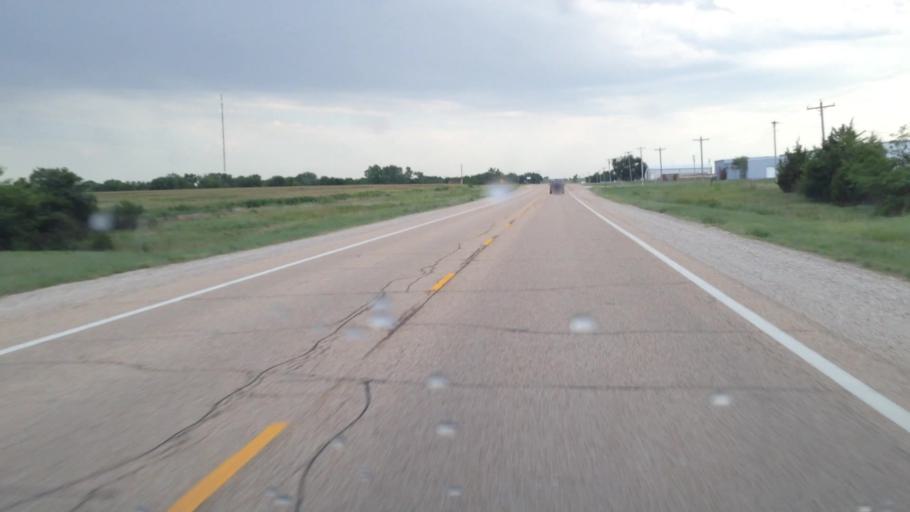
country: US
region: Kansas
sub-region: Coffey County
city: Burlington
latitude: 38.1735
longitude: -95.7389
